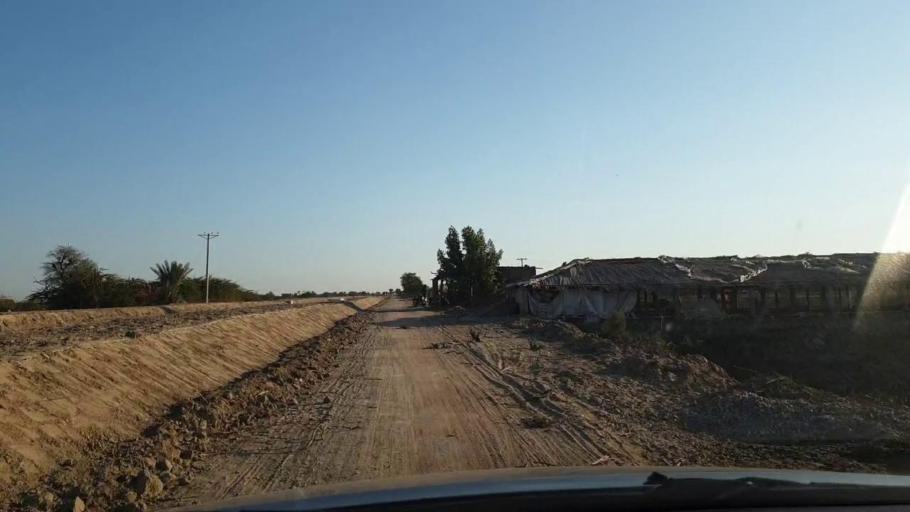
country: PK
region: Sindh
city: Tando Mittha Khan
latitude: 25.8399
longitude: 69.1730
